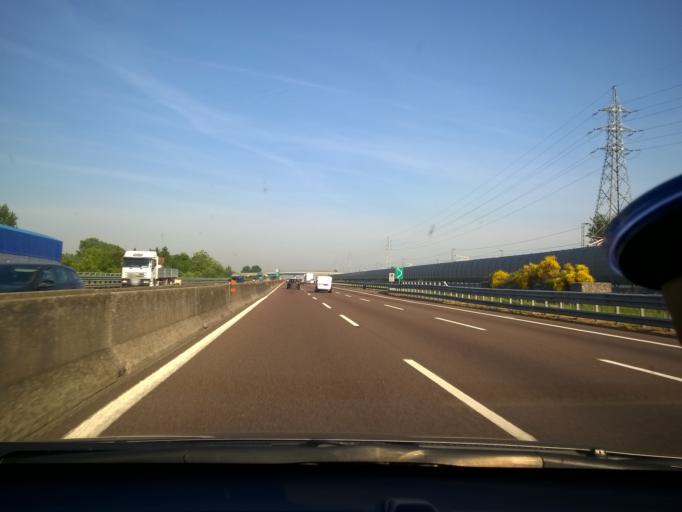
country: IT
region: Emilia-Romagna
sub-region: Provincia di Reggio Emilia
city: Rubiera
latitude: 44.6811
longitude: 10.8059
